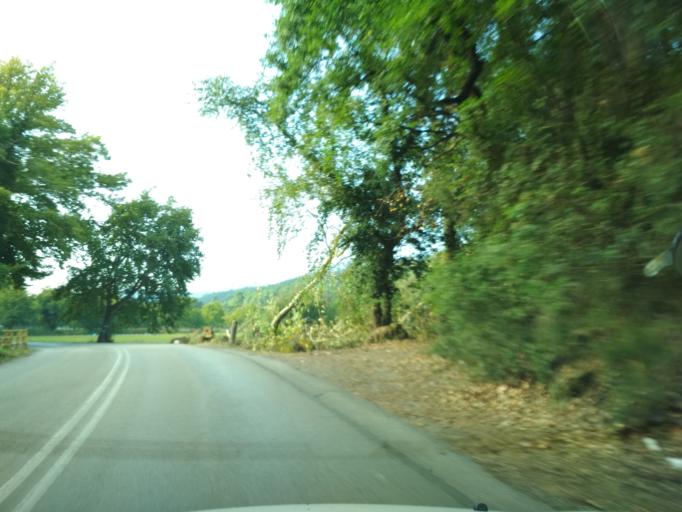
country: GR
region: Central Greece
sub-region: Nomos Evvoias
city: Mantoudi
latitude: 38.7745
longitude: 23.4743
